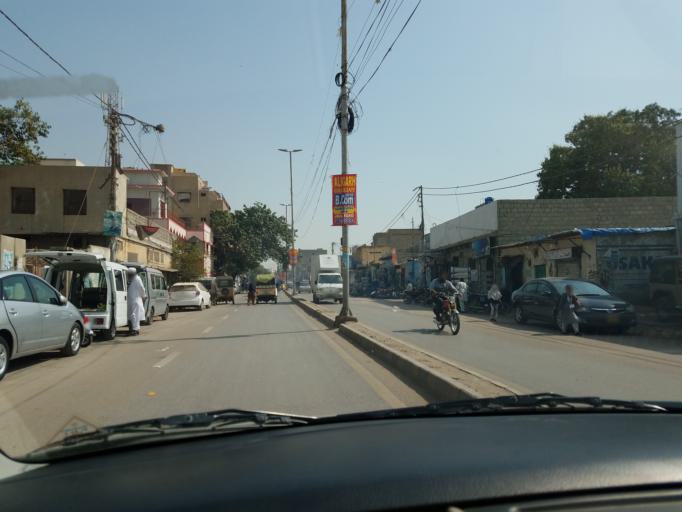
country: PK
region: Sindh
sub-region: Karachi District
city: Karachi
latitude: 24.8908
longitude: 67.0503
